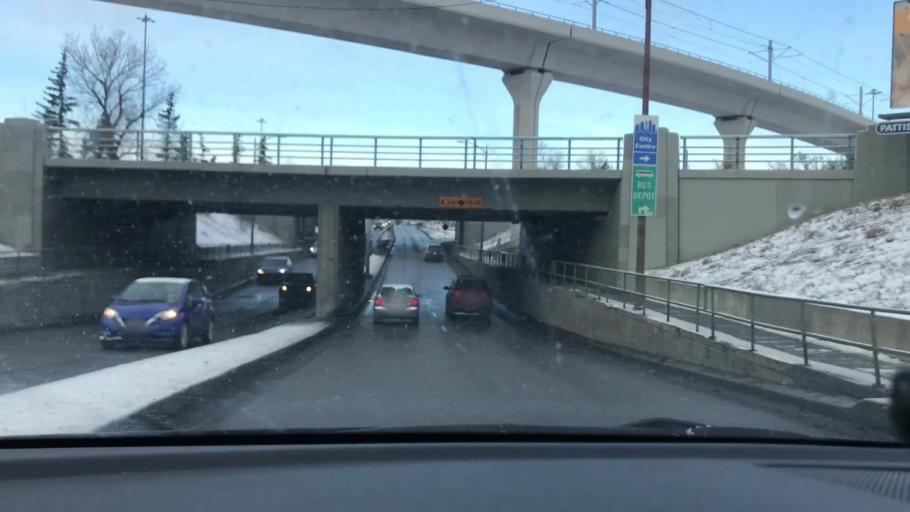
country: CA
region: Alberta
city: Calgary
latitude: 51.0445
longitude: -114.0947
